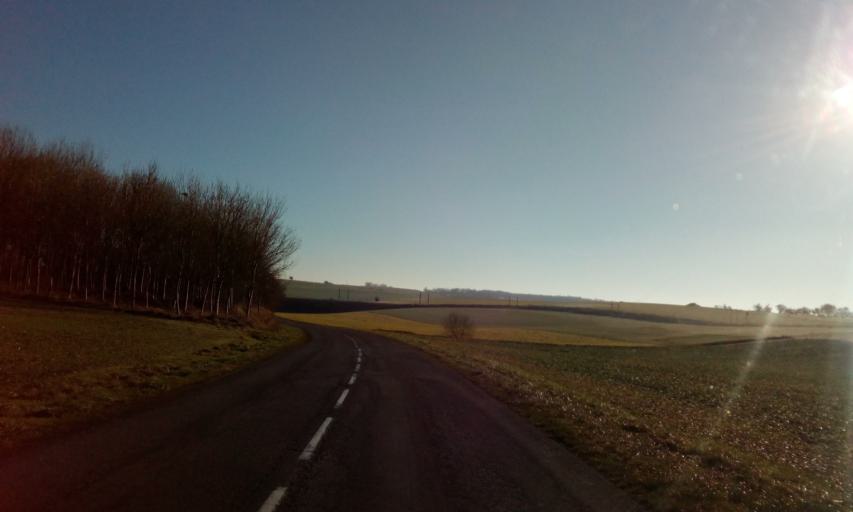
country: FR
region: Champagne-Ardenne
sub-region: Departement des Ardennes
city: Signy-le-Petit
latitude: 49.7794
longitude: 4.3761
